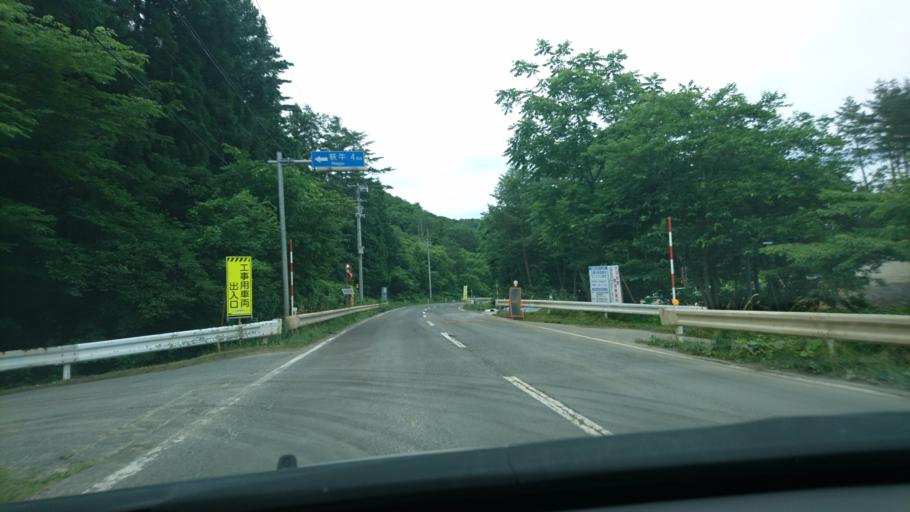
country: JP
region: Iwate
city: Miyako
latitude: 39.9781
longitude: 141.8570
